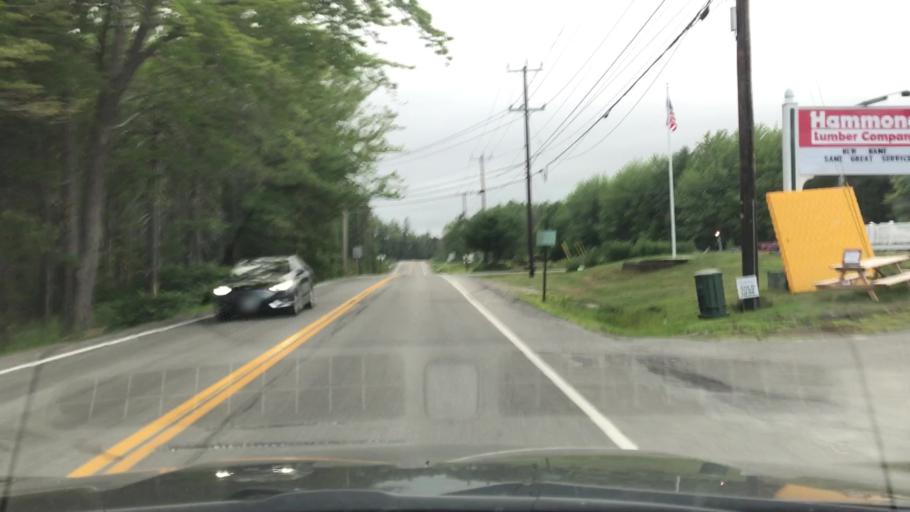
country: US
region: Maine
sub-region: Hancock County
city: Trenton
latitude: 44.4068
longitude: -68.3479
